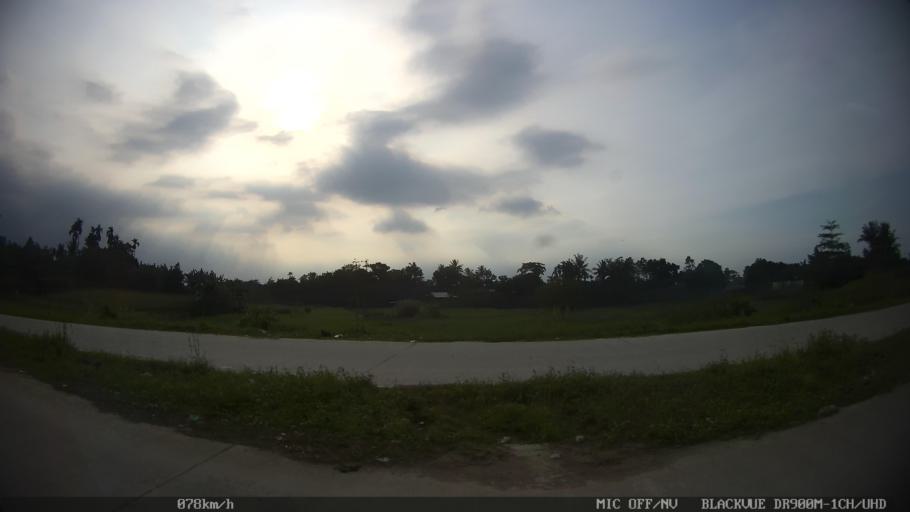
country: ID
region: North Sumatra
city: Binjai
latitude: 3.6008
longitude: 98.5334
